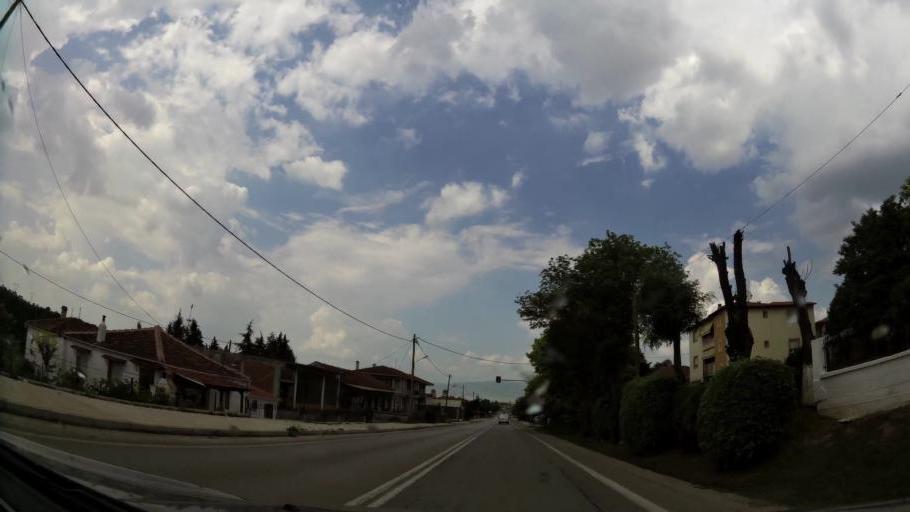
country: GR
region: West Macedonia
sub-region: Nomos Kozanis
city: Koila
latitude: 40.3454
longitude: 21.8261
